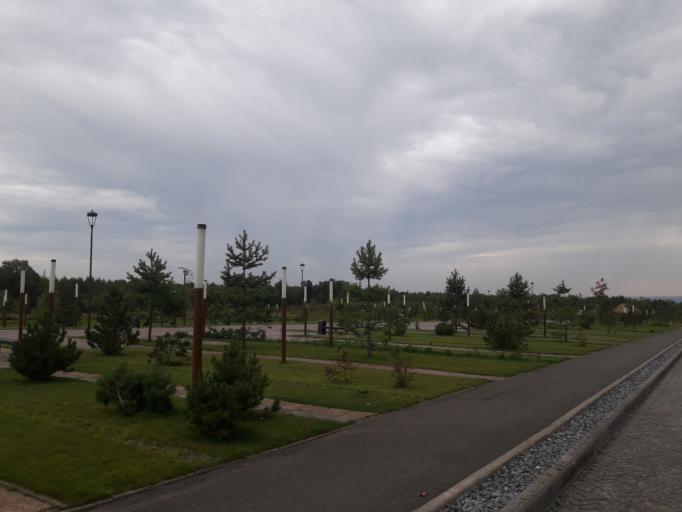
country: RU
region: Tatarstan
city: Sviyazhsk
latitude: 55.7531
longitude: 48.7417
